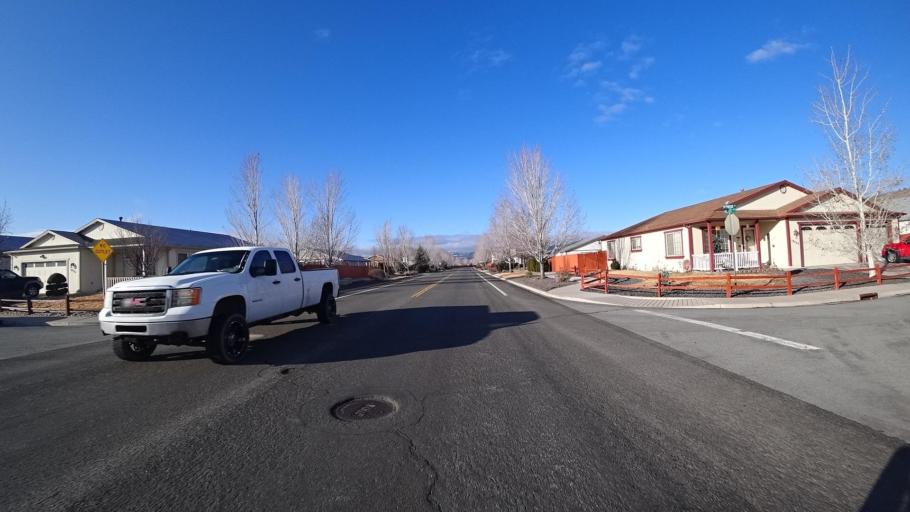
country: US
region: Nevada
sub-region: Washoe County
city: Cold Springs
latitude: 39.6901
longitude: -119.9671
